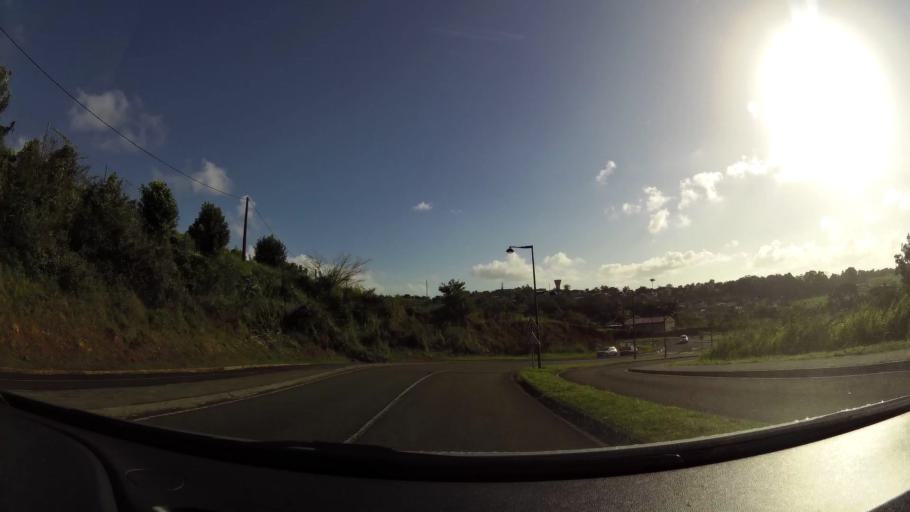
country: MQ
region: Martinique
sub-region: Martinique
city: Saint-Joseph
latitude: 14.6358
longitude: -61.0375
